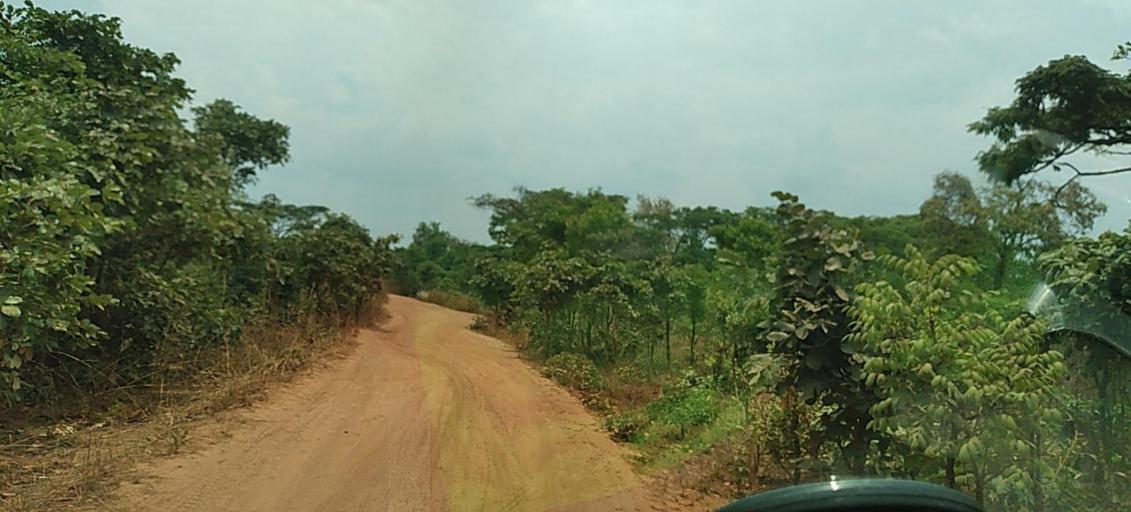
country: ZM
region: North-Western
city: Kansanshi
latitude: -12.0507
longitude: 26.3403
